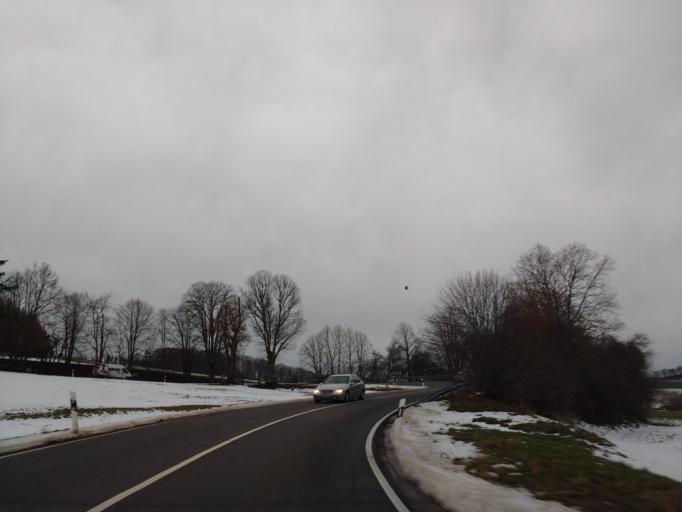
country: DE
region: Thuringia
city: Siemerode
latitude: 51.4110
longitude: 10.1224
